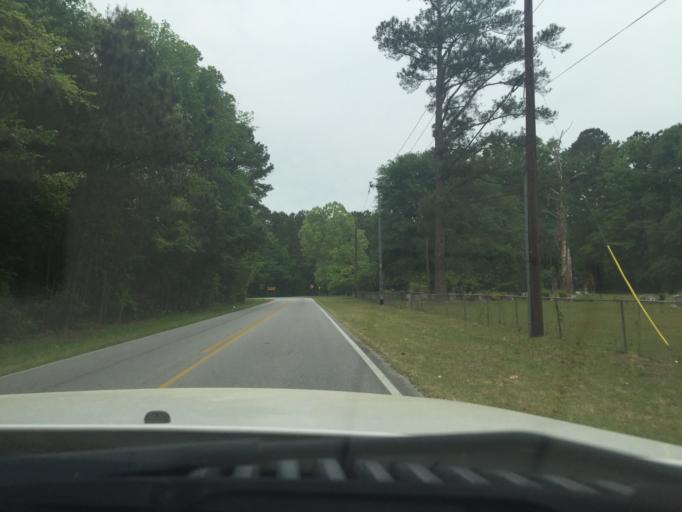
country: US
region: Georgia
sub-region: Chatham County
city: Georgetown
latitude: 31.9696
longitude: -81.2422
